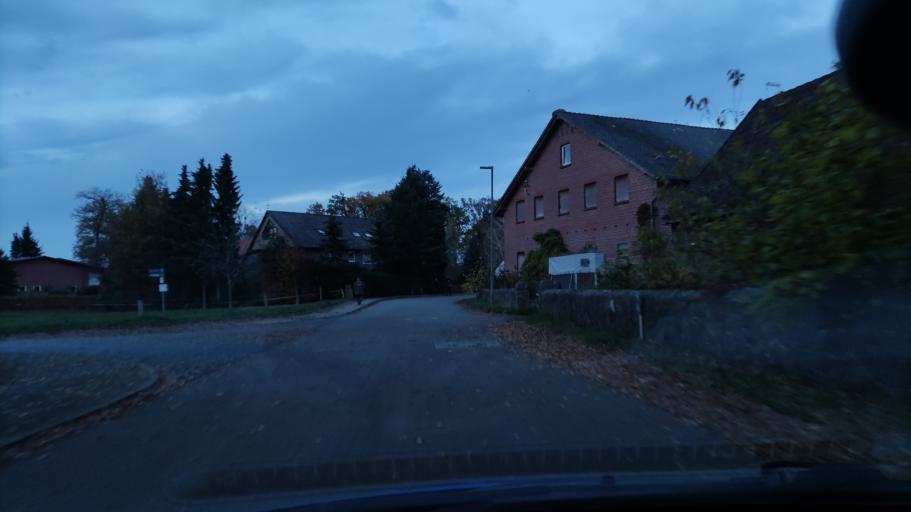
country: DE
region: Lower Saxony
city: Egestorf
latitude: 53.1414
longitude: 10.0298
